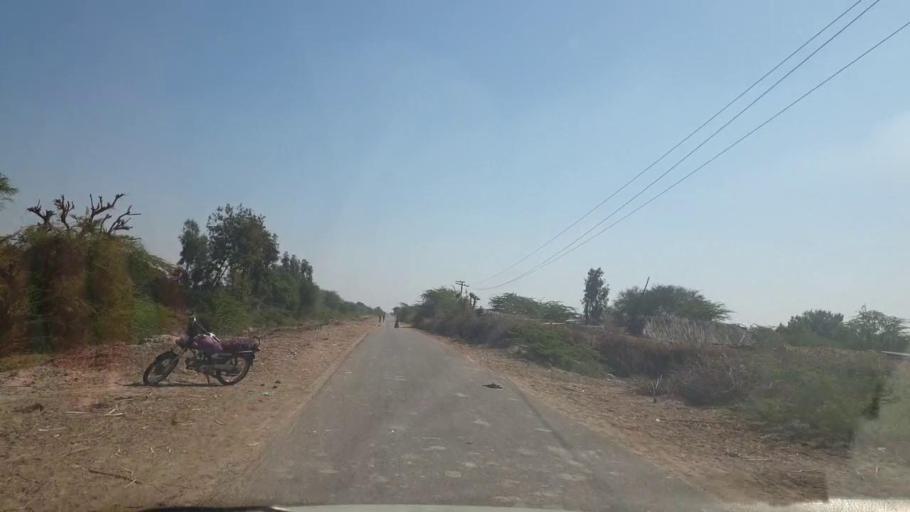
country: PK
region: Sindh
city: Mirpur Khas
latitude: 25.4799
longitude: 69.1723
